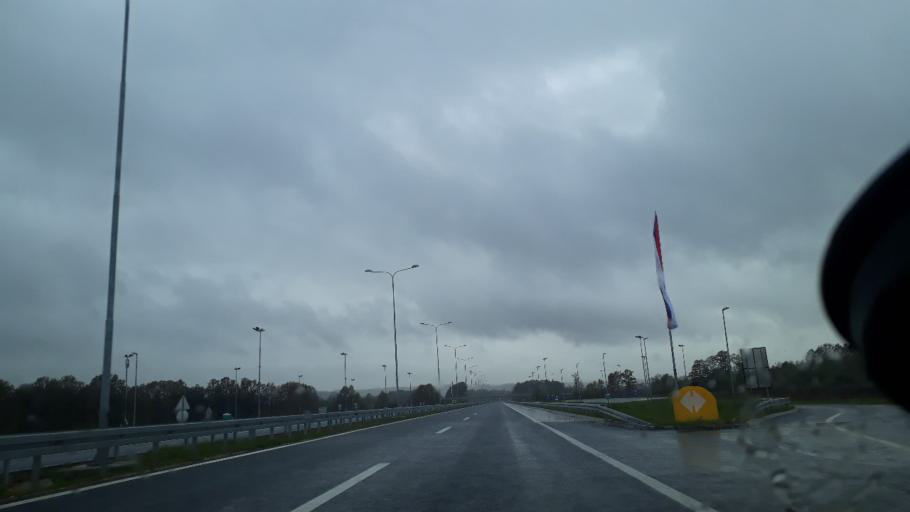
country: BA
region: Republika Srpska
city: Stanari
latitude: 44.8158
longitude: 17.9032
